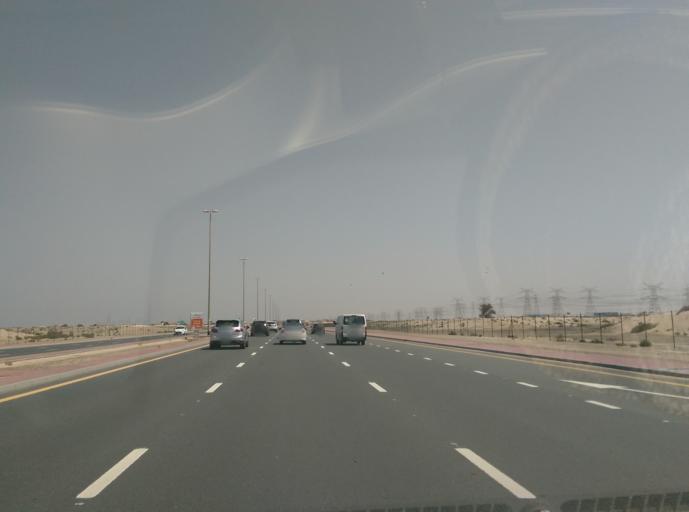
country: AE
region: Dubai
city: Dubai
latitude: 25.0714
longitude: 55.1961
